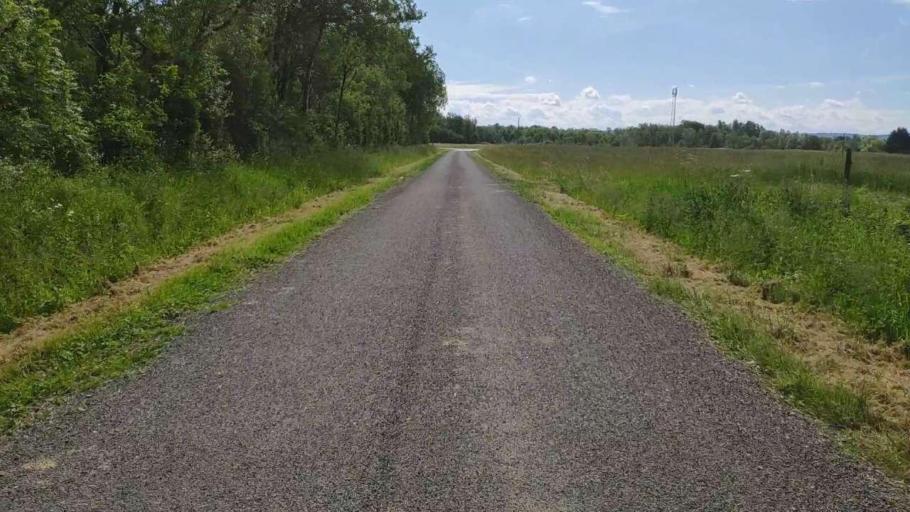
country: FR
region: Franche-Comte
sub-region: Departement du Jura
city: Bletterans
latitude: 46.6795
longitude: 5.4266
